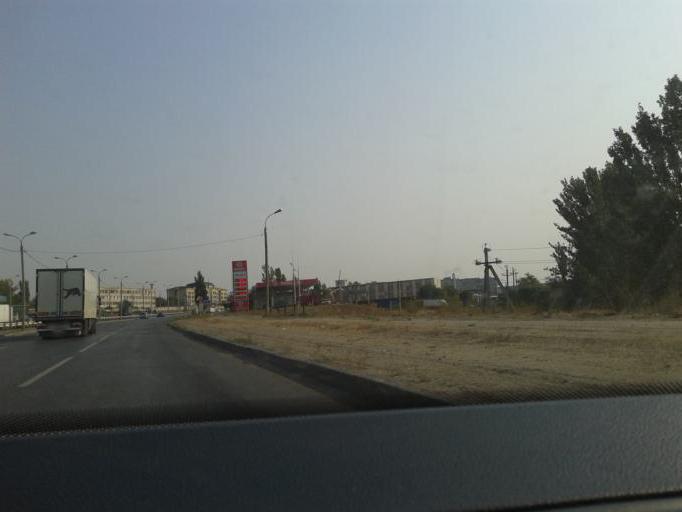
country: RU
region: Volgograd
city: Volgograd
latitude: 48.7471
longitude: 44.4672
